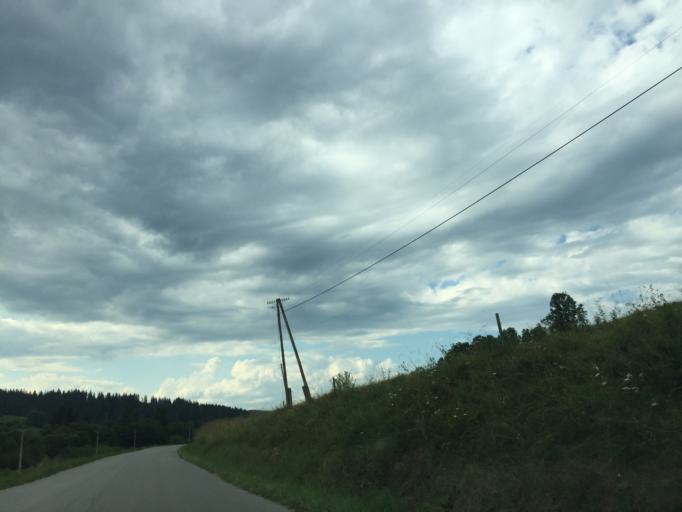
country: PL
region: Silesian Voivodeship
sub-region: Powiat zywiecki
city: Korbielow
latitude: 49.4306
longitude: 19.3205
